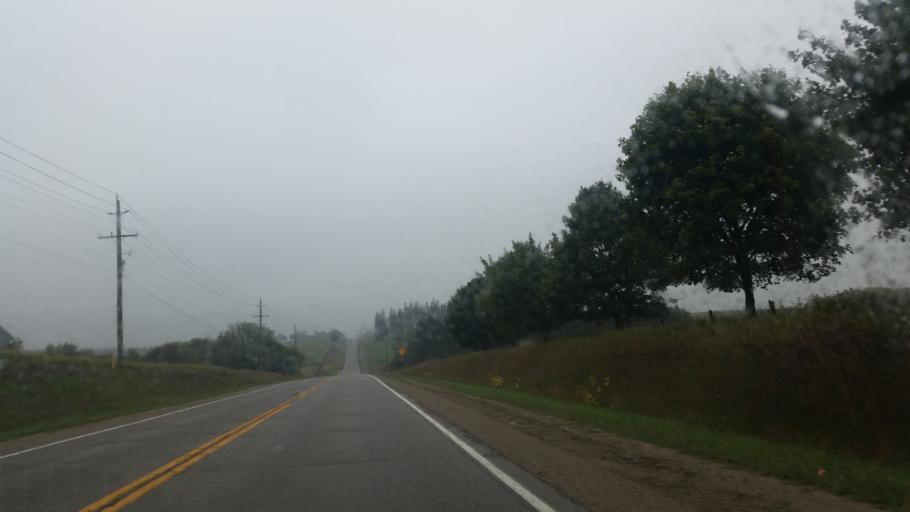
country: CA
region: Ontario
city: Waterloo
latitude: 43.6861
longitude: -80.4558
